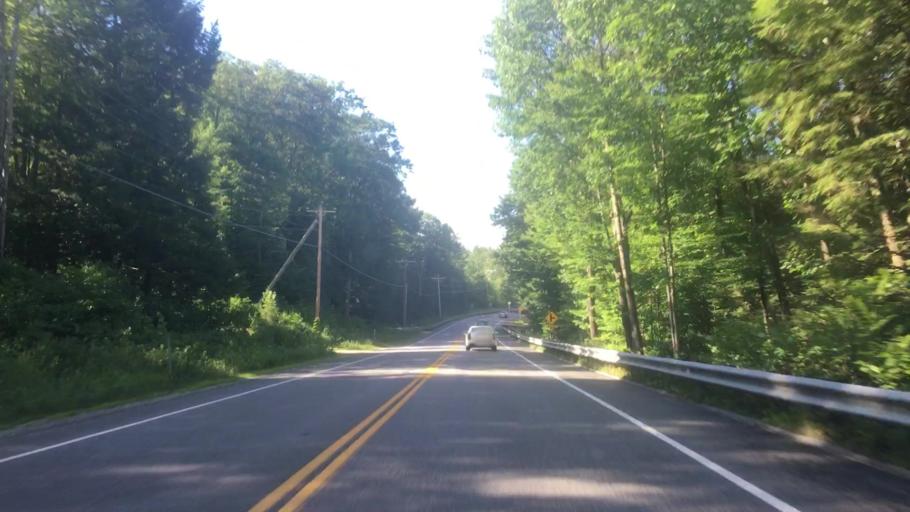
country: US
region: New Hampshire
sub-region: Hillsborough County
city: Hillsborough
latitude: 43.1062
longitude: -71.9566
